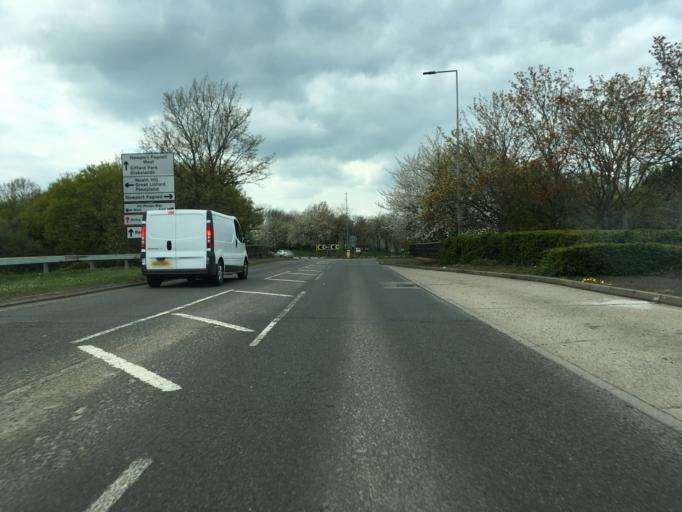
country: GB
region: England
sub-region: Milton Keynes
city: Newport Pagnell
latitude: 52.0659
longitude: -0.7378
